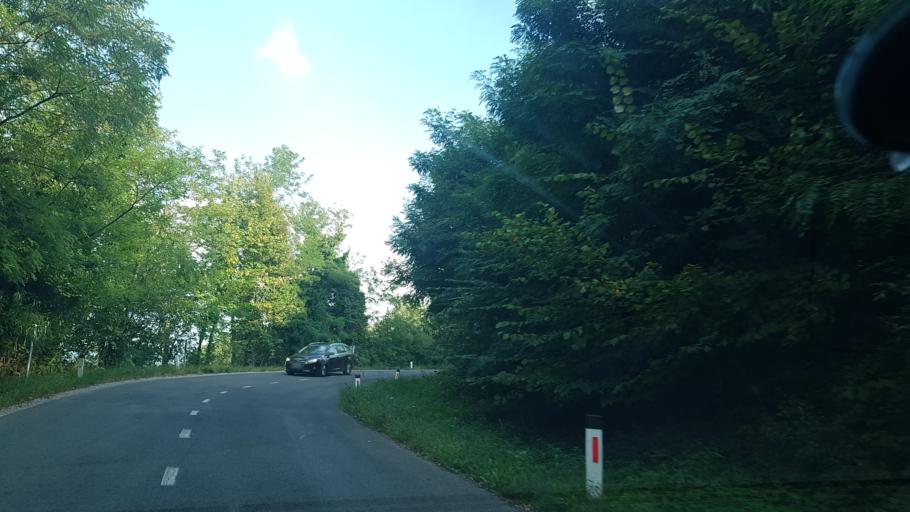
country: SI
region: Nova Gorica
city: Nova Gorica
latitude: 45.9501
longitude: 13.6429
